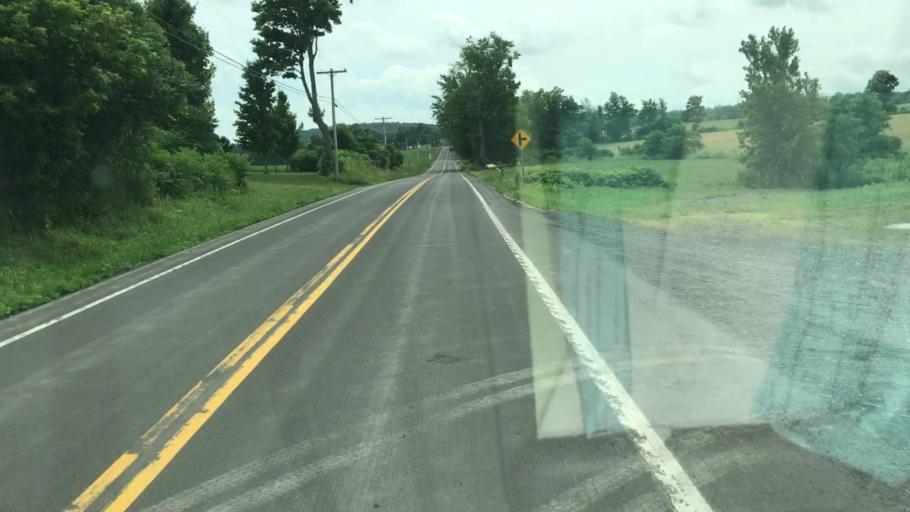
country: US
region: New York
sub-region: Onondaga County
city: Manlius
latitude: 42.9304
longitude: -75.9765
